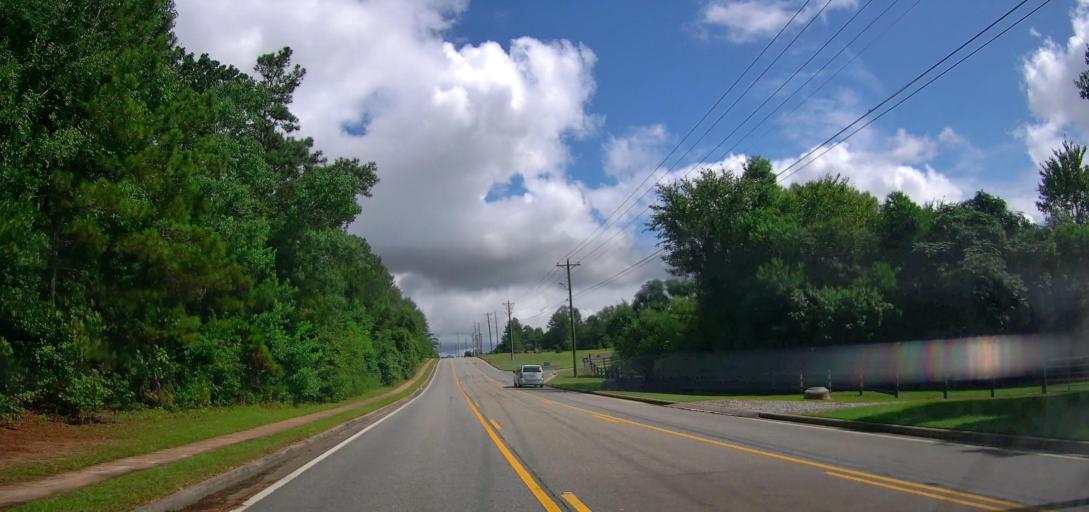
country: US
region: Georgia
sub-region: Houston County
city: Warner Robins
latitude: 32.5891
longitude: -83.6371
